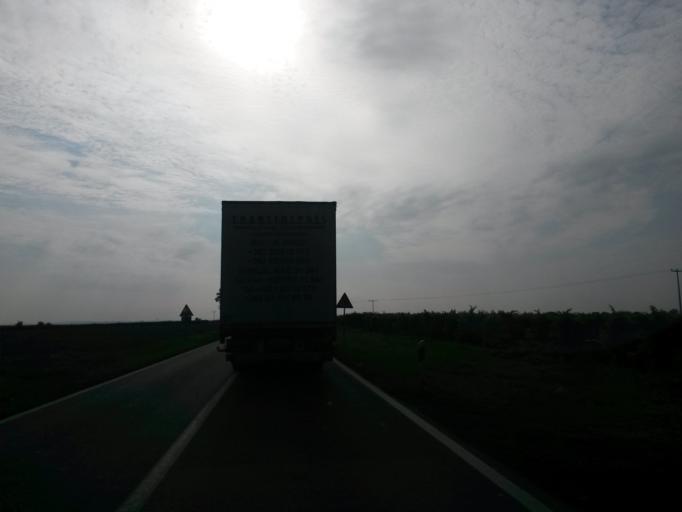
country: HR
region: Vukovarsko-Srijemska
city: Lovas
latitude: 45.2477
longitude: 19.2235
